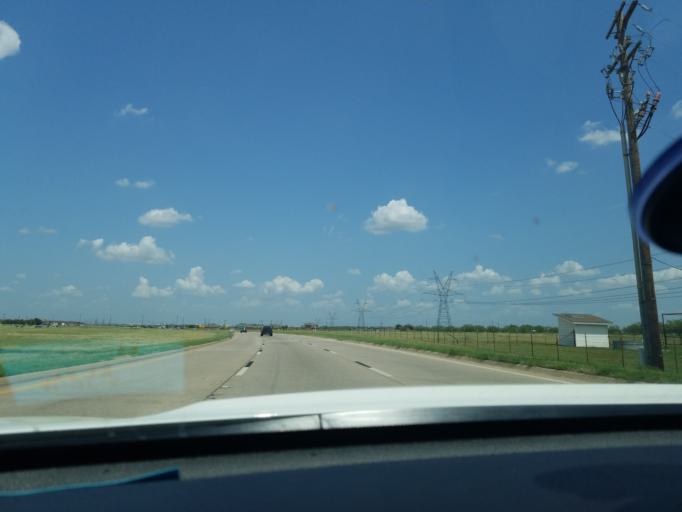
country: US
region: Texas
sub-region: Tarrant County
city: Haslet
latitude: 32.9592
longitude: -97.3047
